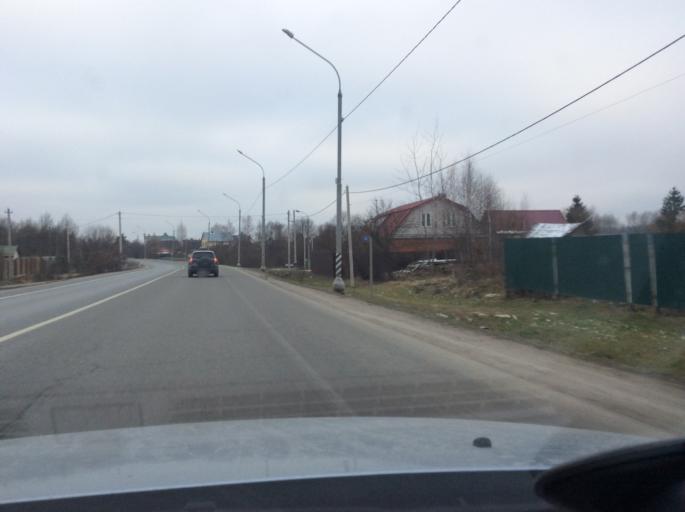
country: RU
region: Moskovskaya
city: Troitsk
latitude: 55.3723
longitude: 37.2040
